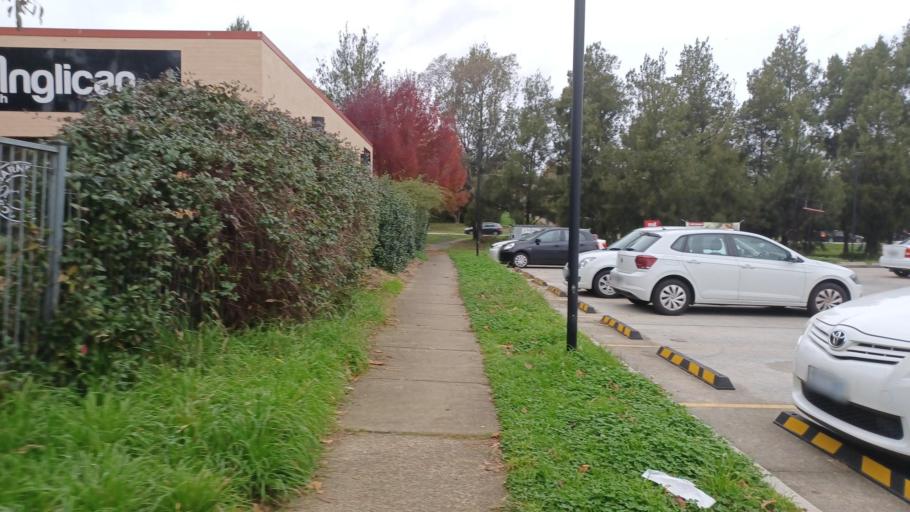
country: AU
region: Australian Capital Territory
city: Belconnen
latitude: -35.2054
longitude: 149.0345
